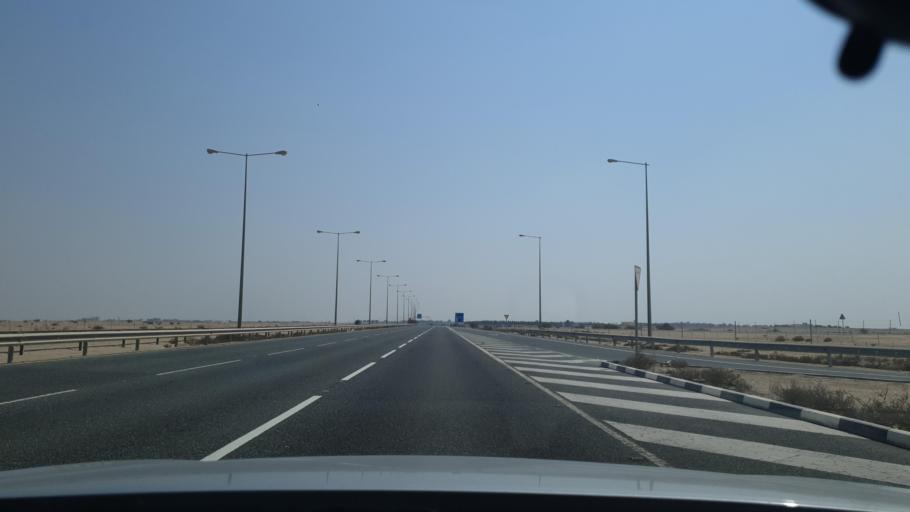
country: QA
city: Al Ghuwayriyah
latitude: 25.7973
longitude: 51.3854
